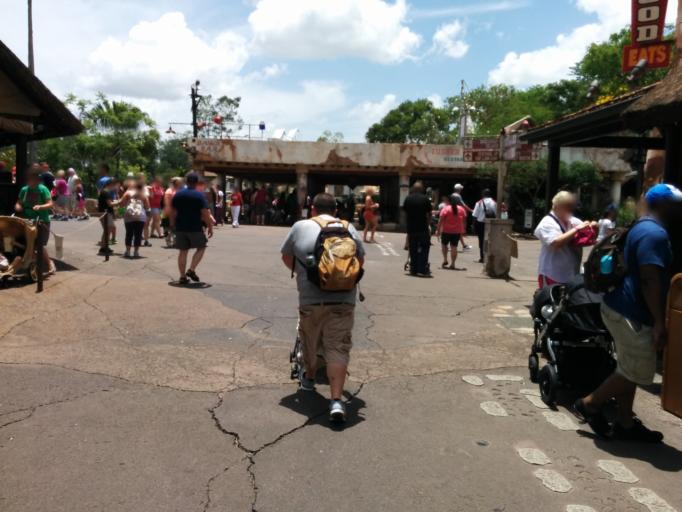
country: US
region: Florida
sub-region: Polk County
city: Citrus Ridge
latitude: 28.3586
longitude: -81.5916
